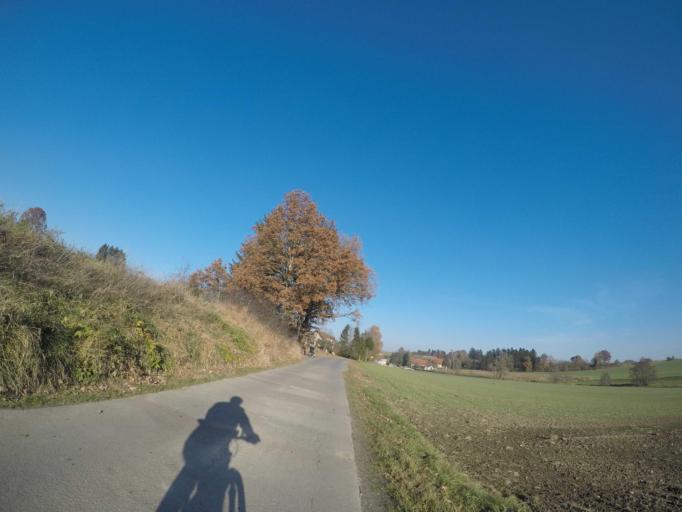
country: DE
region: Baden-Wuerttemberg
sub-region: Tuebingen Region
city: Oberstadion
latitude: 48.1874
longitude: 9.6758
